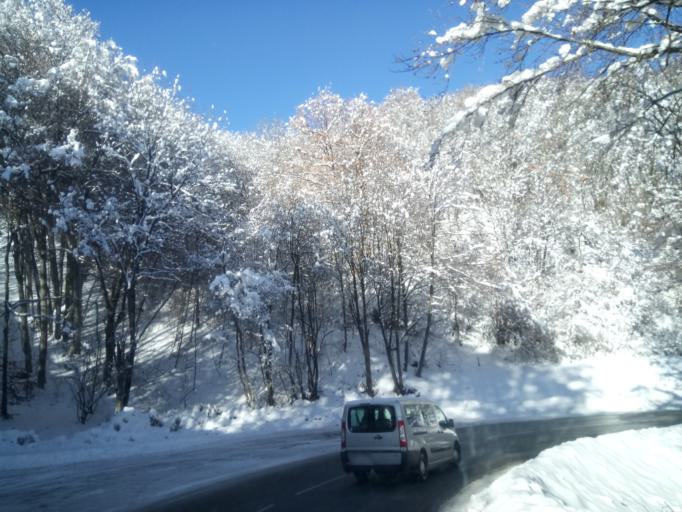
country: FR
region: Rhone-Alpes
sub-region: Departement de la Savoie
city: Saint-Jean-de-Maurienne
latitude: 45.2511
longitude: 6.3134
